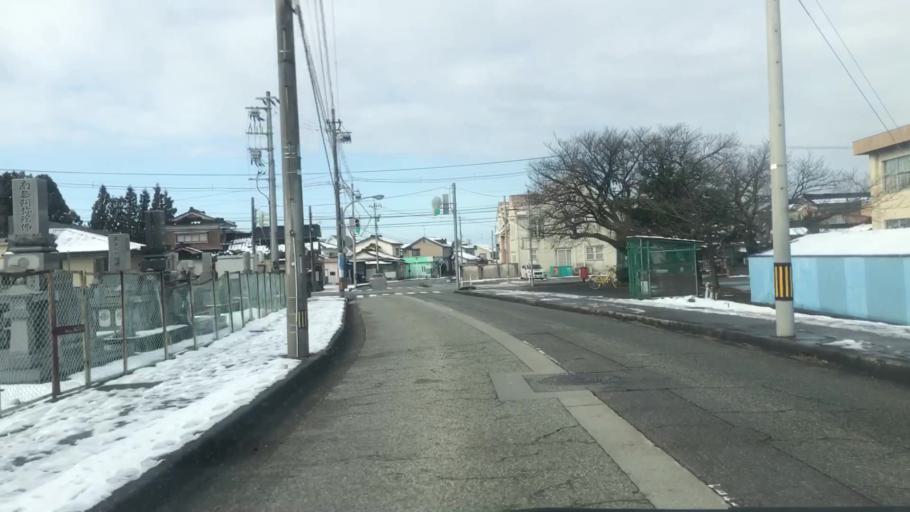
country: JP
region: Toyama
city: Toyama-shi
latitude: 36.6166
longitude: 137.2521
